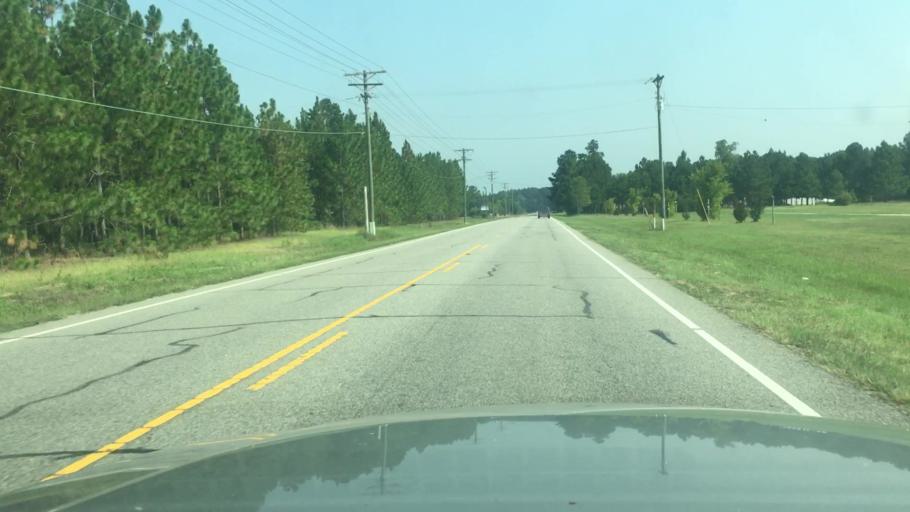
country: US
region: North Carolina
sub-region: Cumberland County
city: Hope Mills
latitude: 34.9058
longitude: -78.9029
